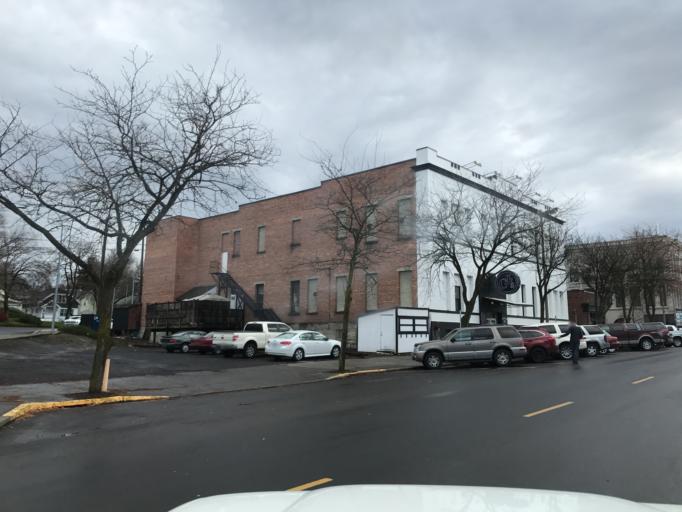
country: US
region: Idaho
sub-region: Latah County
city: Moscow
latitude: 46.7345
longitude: -117.0015
